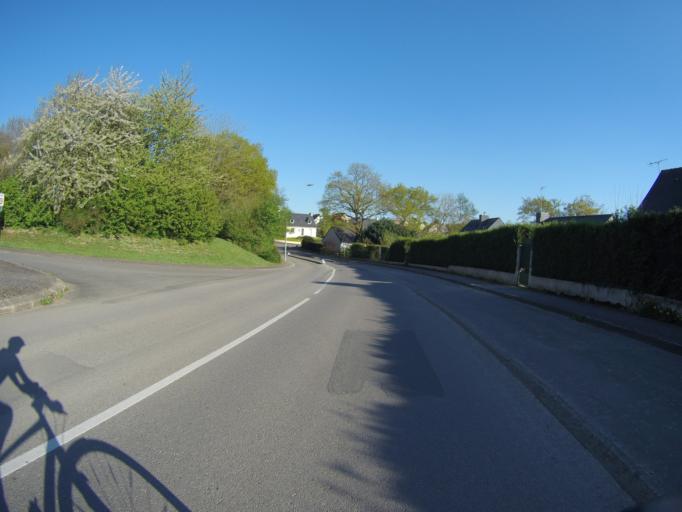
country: FR
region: Brittany
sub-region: Departement d'Ille-et-Vilaine
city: Vern-sur-Seiche
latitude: 48.0420
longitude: -1.5949
